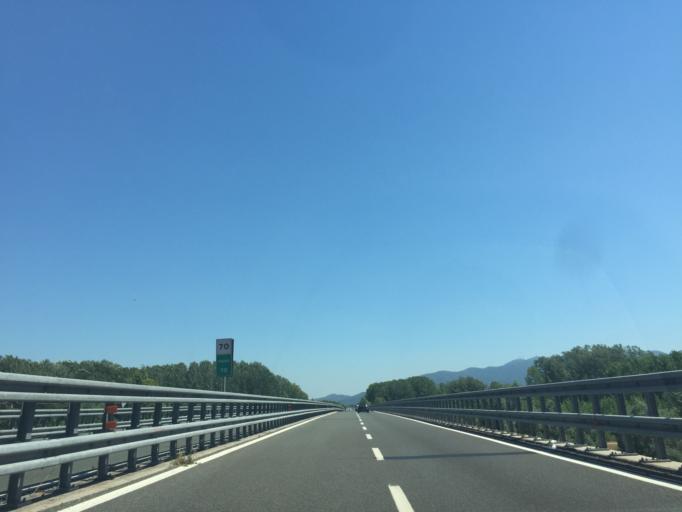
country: IT
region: Tuscany
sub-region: Provincia di Lucca
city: Lucca
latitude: 43.8477
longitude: 10.4460
